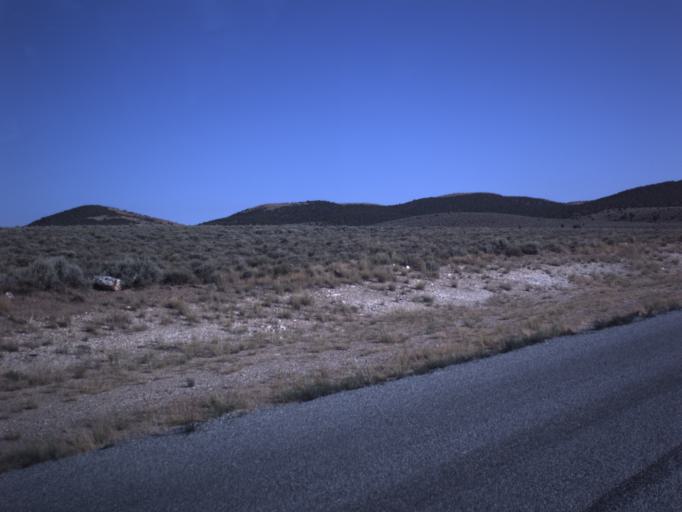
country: US
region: Utah
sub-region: Iron County
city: Parowan
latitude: 38.0284
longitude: -112.9982
